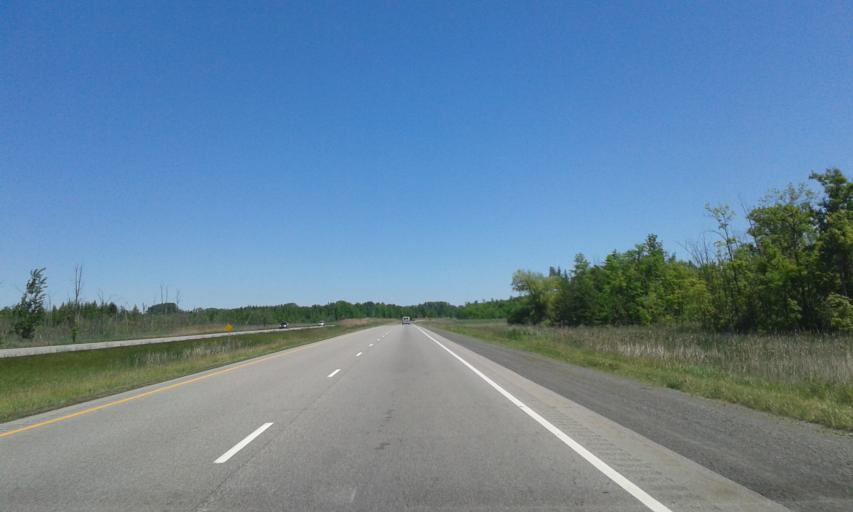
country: CA
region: Ontario
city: Prescott
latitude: 44.7701
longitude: -75.4621
